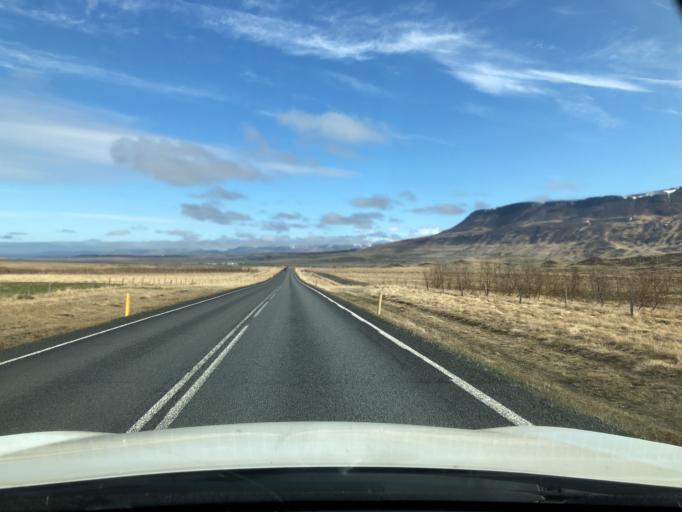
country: IS
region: Northwest
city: Saudarkrokur
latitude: 65.4956
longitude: -20.4076
